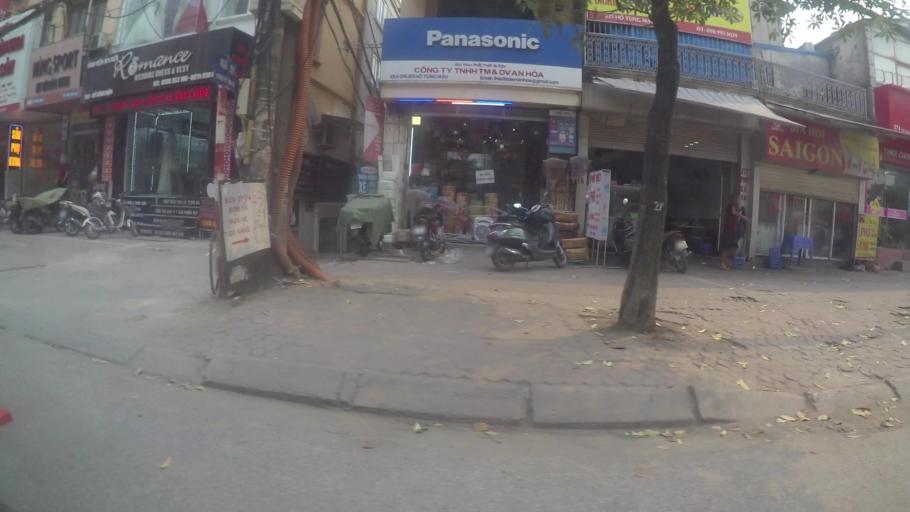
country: VN
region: Ha Noi
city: Cau Dien
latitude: 21.0412
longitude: 105.7622
